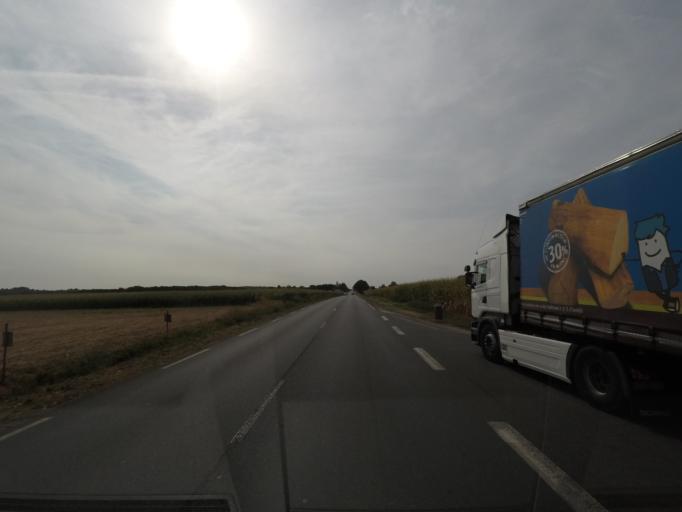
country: FR
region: Poitou-Charentes
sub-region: Departement des Deux-Sevres
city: Sauze-Vaussais
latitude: 46.1367
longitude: 0.1621
